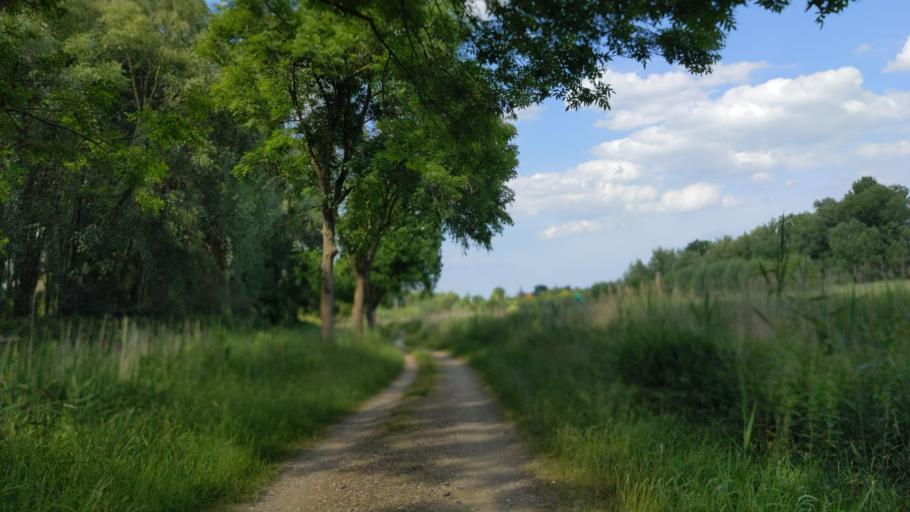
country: DE
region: Schleswig-Holstein
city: Krummesse
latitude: 53.8336
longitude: 10.6424
